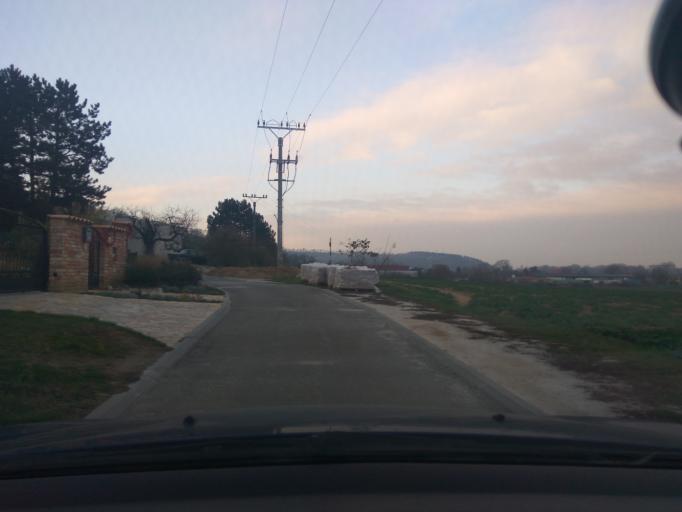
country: SK
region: Trnavsky
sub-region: Okres Trnava
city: Piestany
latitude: 48.5926
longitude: 17.8634
